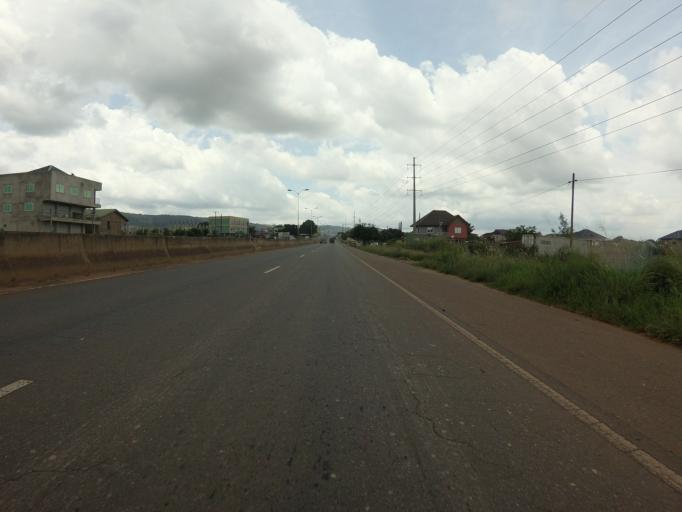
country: GH
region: Eastern
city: Aburi
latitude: 5.7566
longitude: -0.1787
